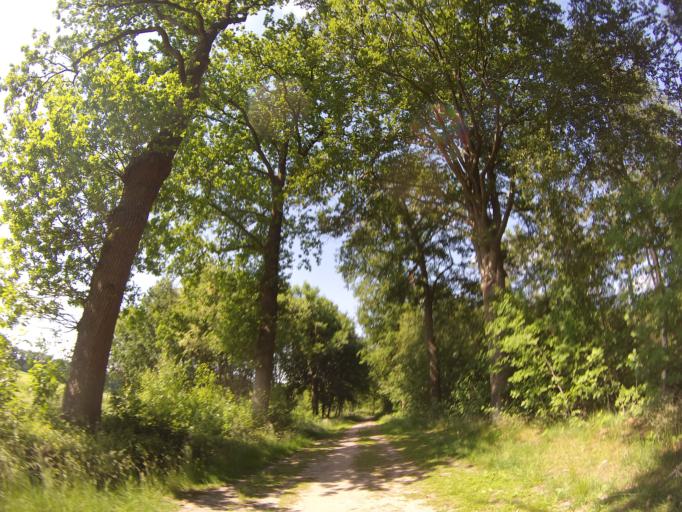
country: NL
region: Gelderland
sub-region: Gemeente Barneveld
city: Terschuur
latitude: 52.1507
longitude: 5.5409
